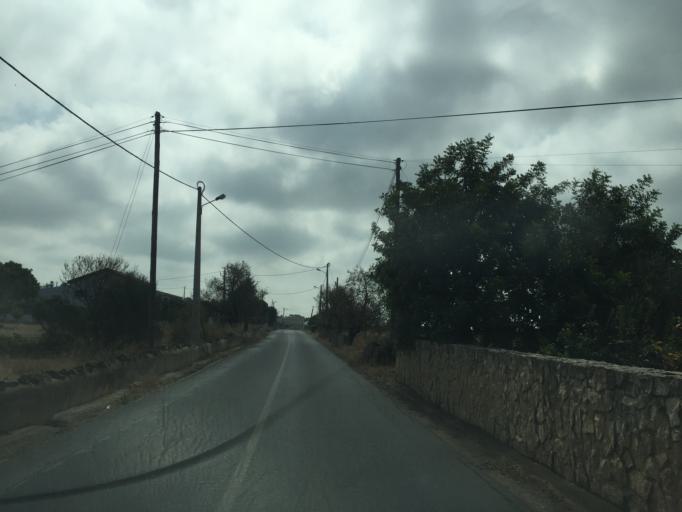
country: PT
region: Faro
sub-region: Olhao
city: Olhao
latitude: 37.0723
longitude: -7.8858
